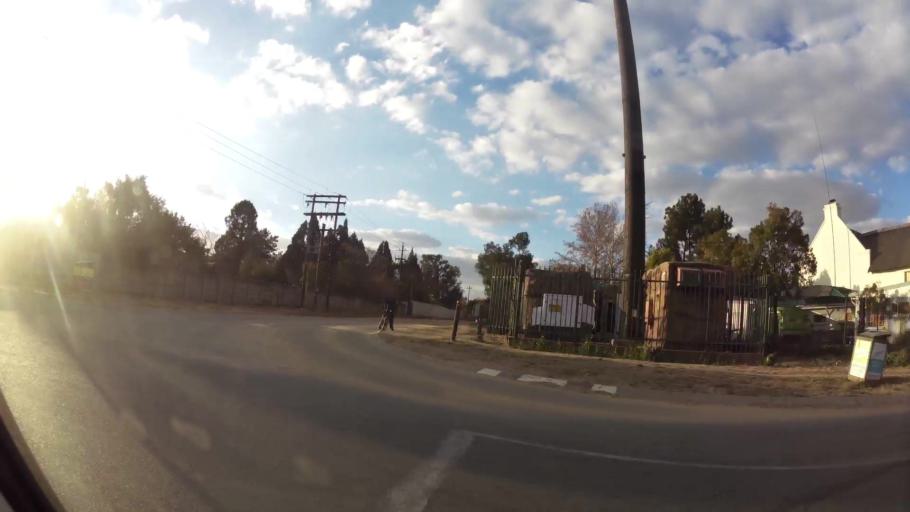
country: ZA
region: Gauteng
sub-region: City of Johannesburg Metropolitan Municipality
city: Diepsloot
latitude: -26.0019
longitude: 27.9814
